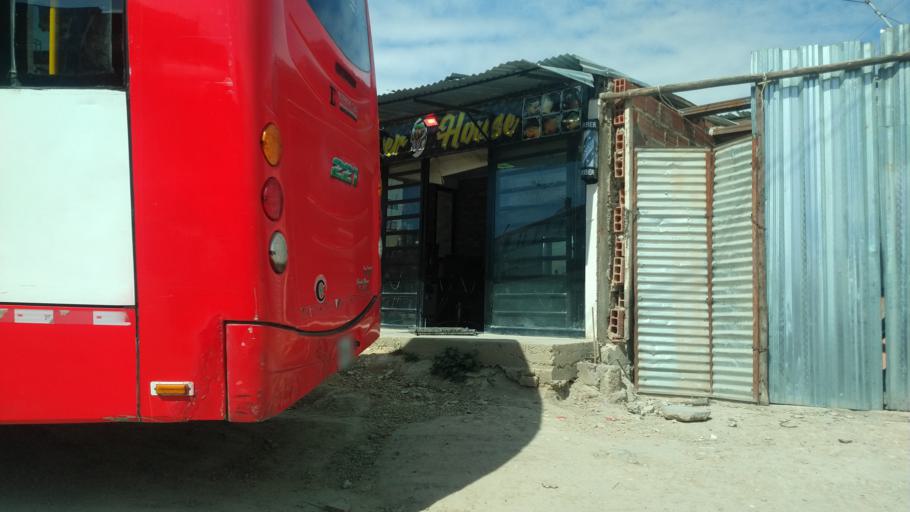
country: CO
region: Cundinamarca
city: Soacha
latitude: 4.5663
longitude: -74.1866
